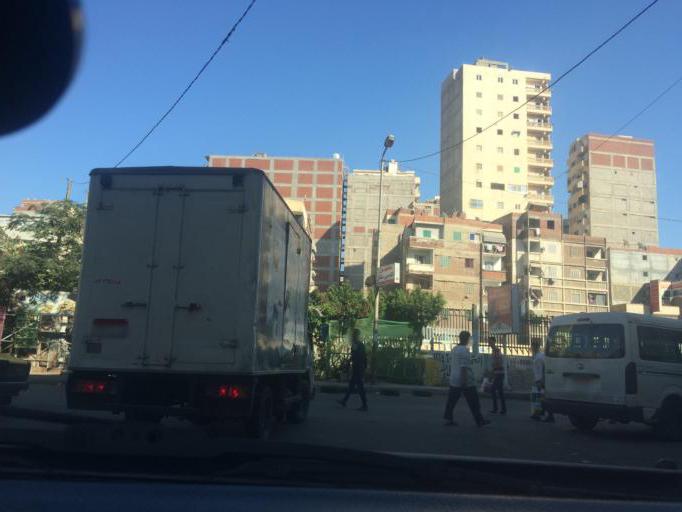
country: EG
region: Alexandria
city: Alexandria
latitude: 31.2597
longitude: 29.9964
